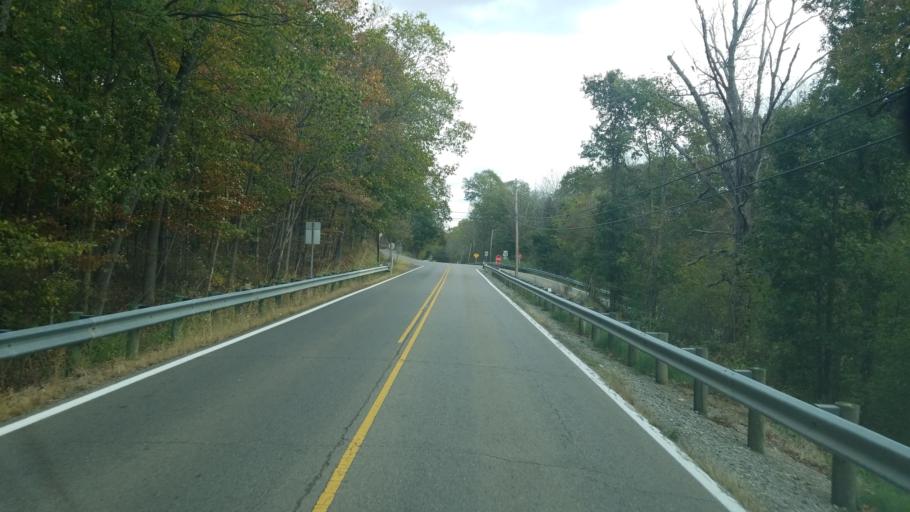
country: US
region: Ohio
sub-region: Jackson County
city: Wellston
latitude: 39.1167
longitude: -82.5608
